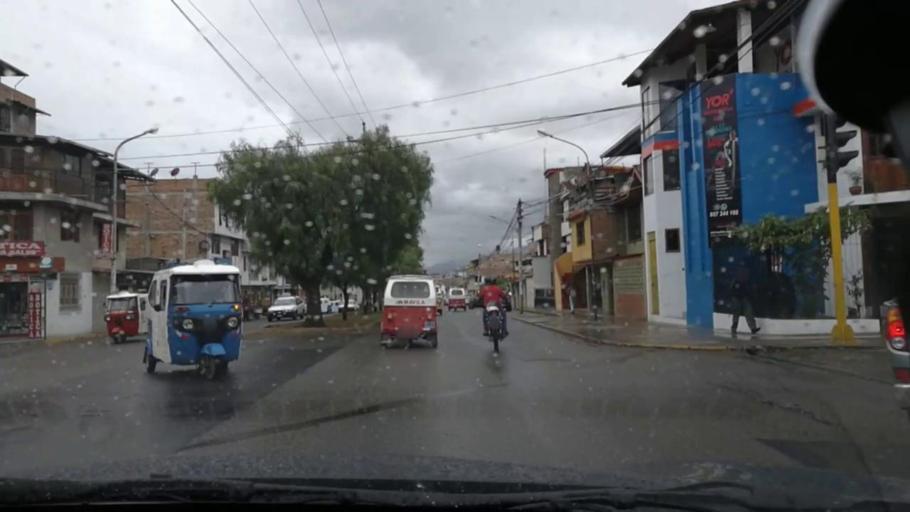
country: PE
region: Cajamarca
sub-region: Provincia de Cajamarca
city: Cajamarca
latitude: -7.1598
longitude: -78.5090
